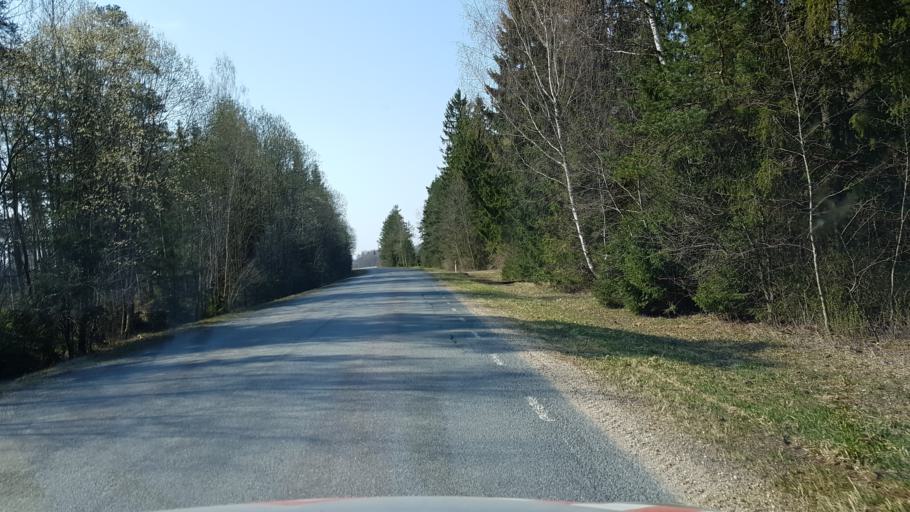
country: EE
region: Raplamaa
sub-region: Maerjamaa vald
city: Marjamaa
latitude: 58.8873
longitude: 24.3919
